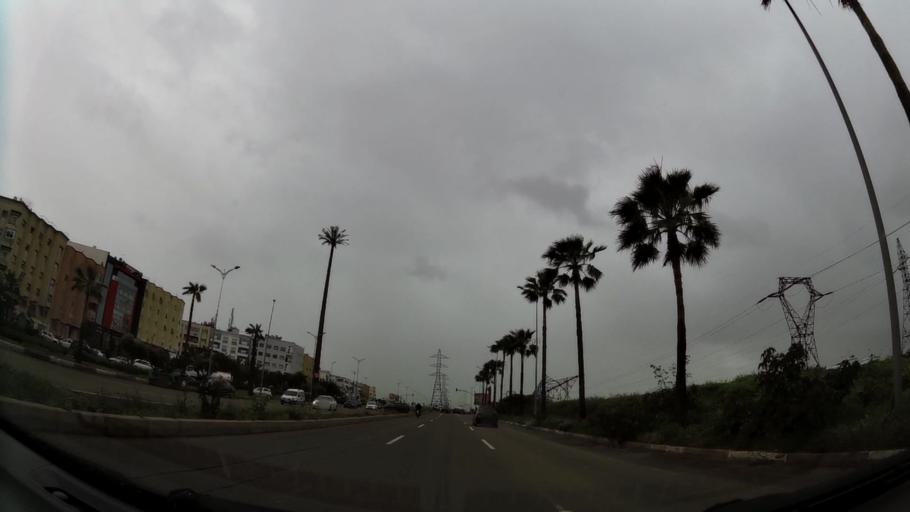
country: MA
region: Grand Casablanca
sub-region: Casablanca
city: Casablanca
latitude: 33.5331
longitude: -7.6175
